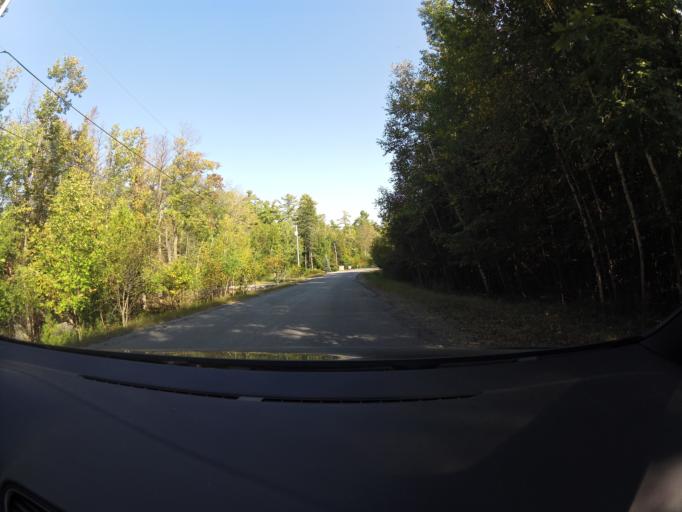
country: CA
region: Ontario
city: Arnprior
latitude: 45.4627
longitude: -76.2825
